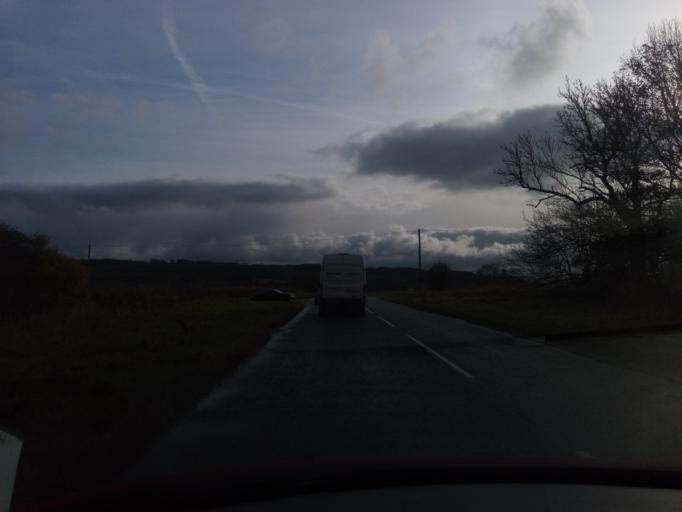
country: GB
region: England
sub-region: Northumberland
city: Wall
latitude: 55.0374
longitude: -2.1368
